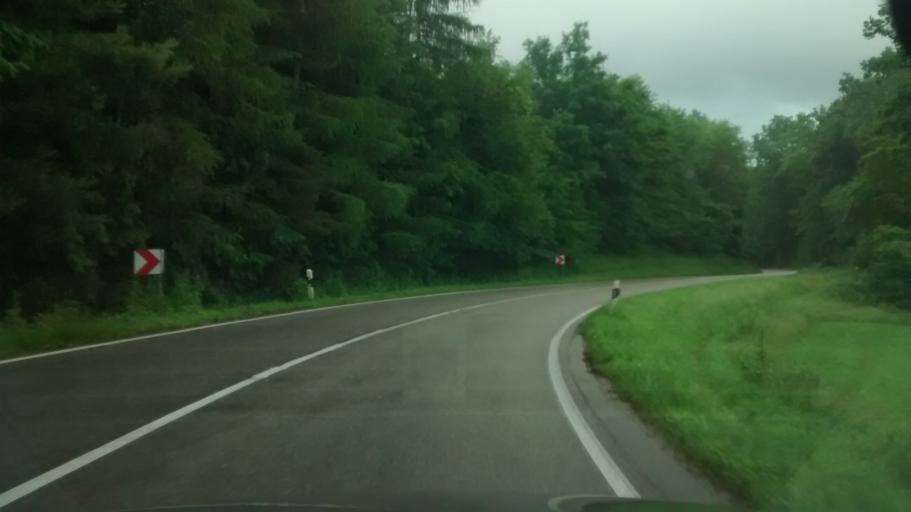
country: DE
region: Rheinland-Pfalz
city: Vorderweidenthal
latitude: 49.1205
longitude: 7.8588
